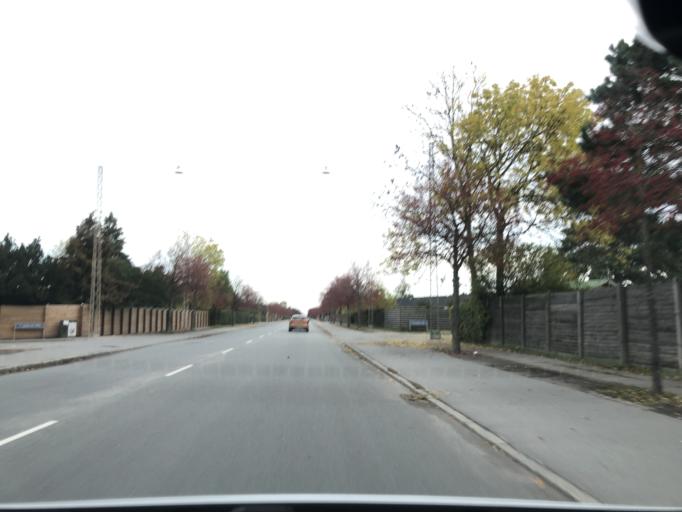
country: DK
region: Capital Region
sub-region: Tarnby Kommune
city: Tarnby
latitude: 55.5920
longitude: 12.5815
